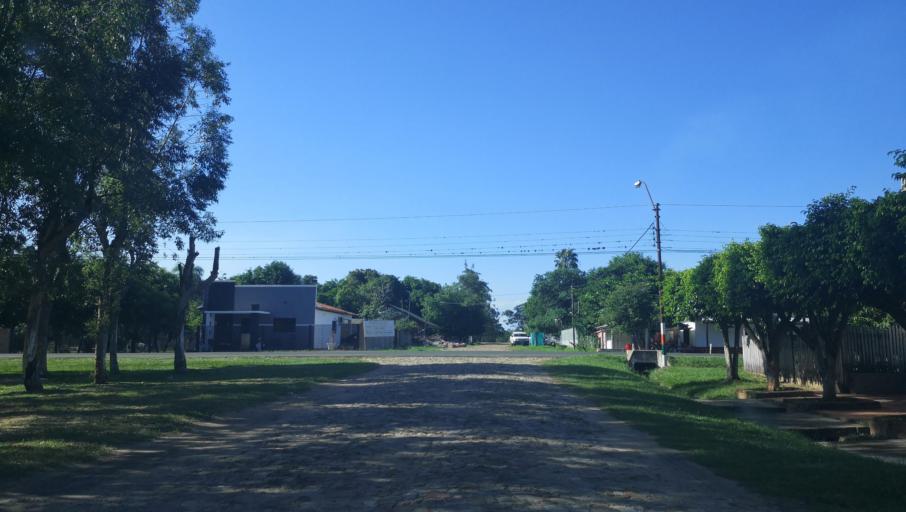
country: PY
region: Caaguazu
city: Carayao
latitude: -25.1963
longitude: -56.4011
